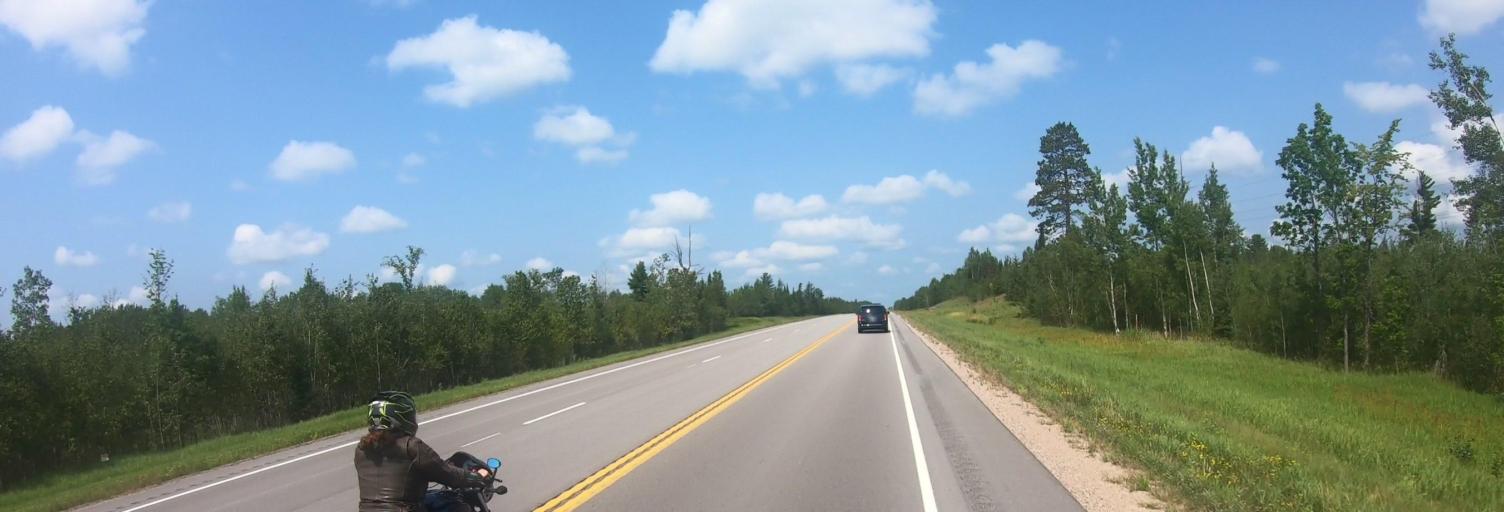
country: US
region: Minnesota
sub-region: Saint Louis County
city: Mountain Iron
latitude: 47.9011
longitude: -92.7880
